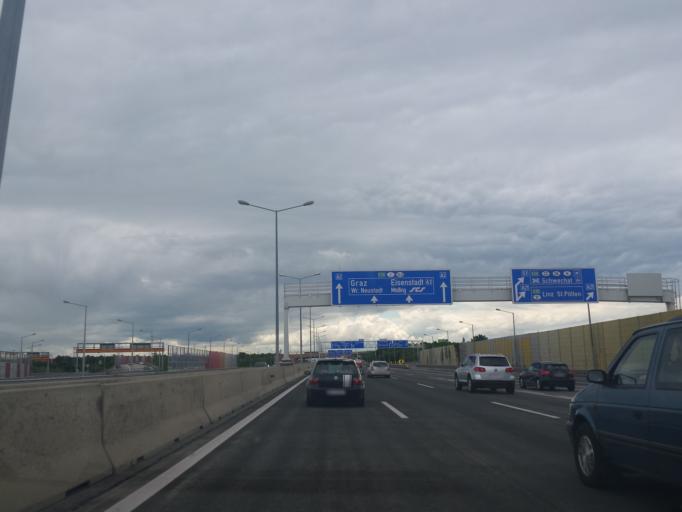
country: AT
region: Lower Austria
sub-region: Politischer Bezirk Modling
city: Vosendorf
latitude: 48.1256
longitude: 16.3269
